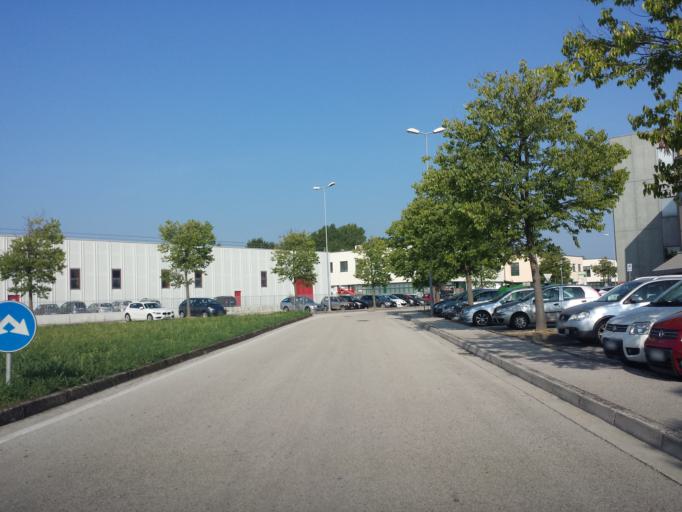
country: IT
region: Veneto
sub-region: Provincia di Vicenza
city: Villaggio Montegrappa
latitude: 45.5238
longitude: 11.5913
